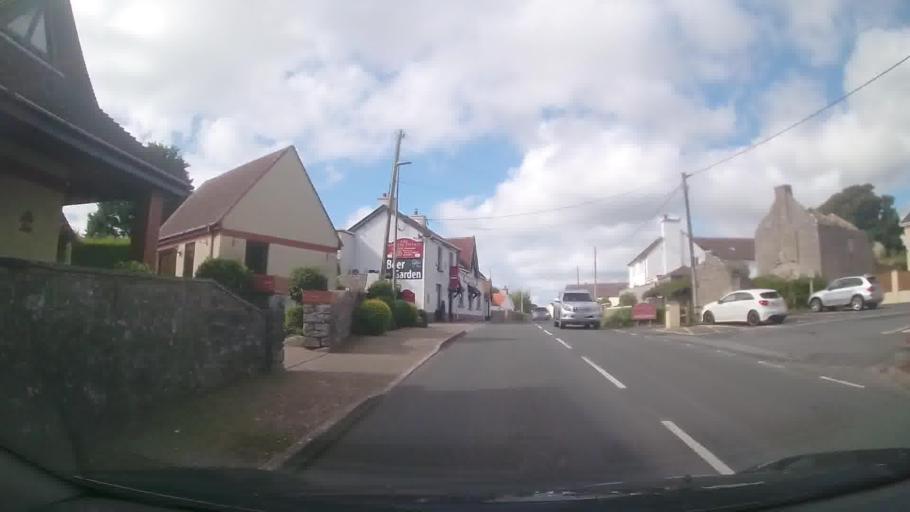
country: GB
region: Wales
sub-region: Pembrokeshire
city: Manorbier
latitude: 51.6512
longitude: -4.7673
